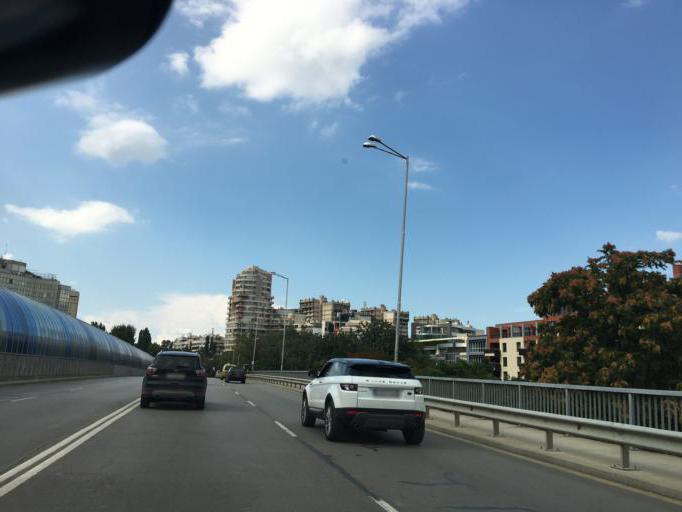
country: BG
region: Sofia-Capital
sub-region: Stolichna Obshtina
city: Sofia
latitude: 42.6681
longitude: 23.3529
